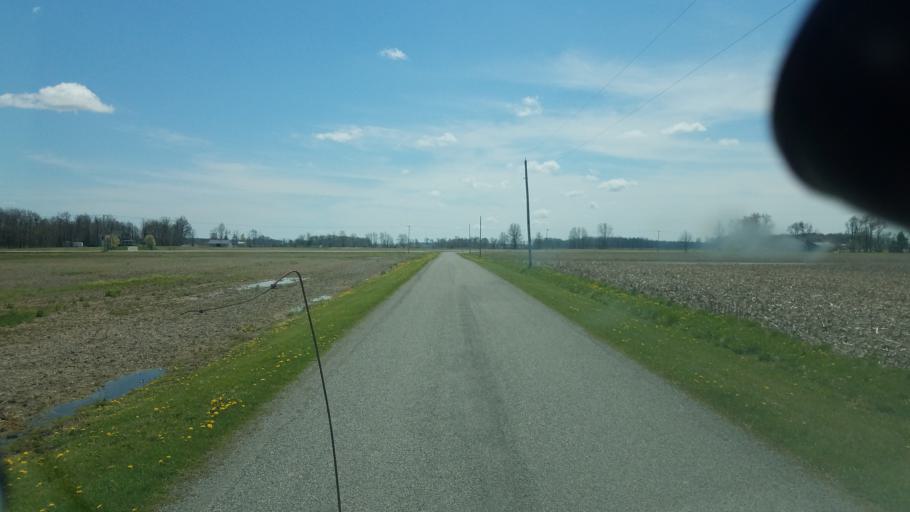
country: US
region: Ohio
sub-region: Union County
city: Richwood
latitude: 40.5020
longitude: -83.2900
